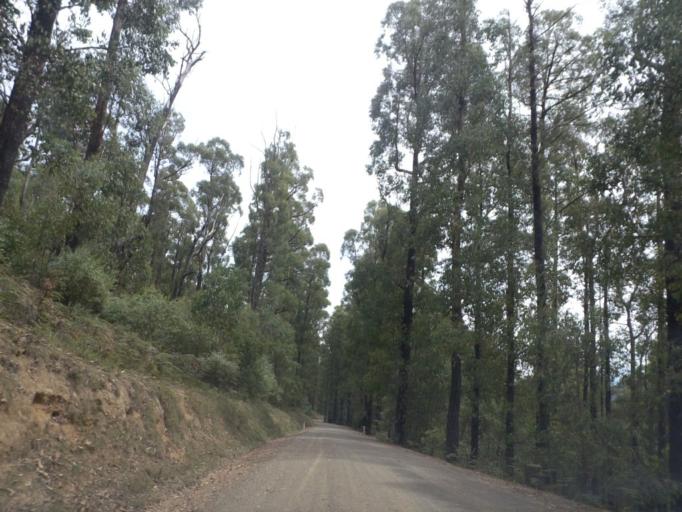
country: AU
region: Victoria
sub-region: Yarra Ranges
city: Healesville
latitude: -37.4376
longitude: 145.5753
